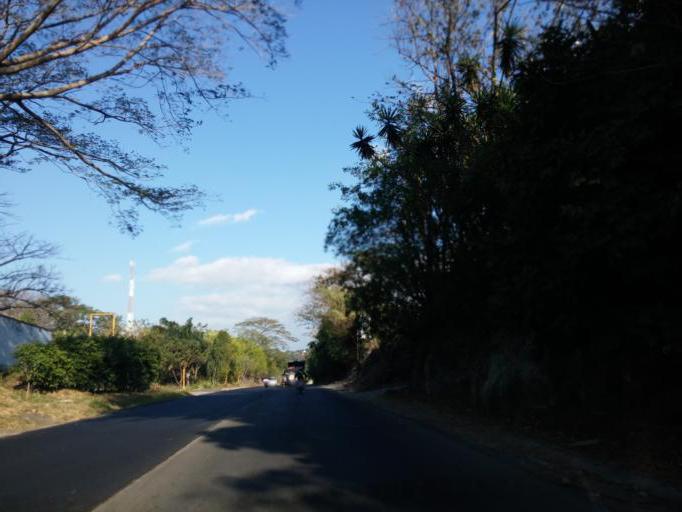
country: CR
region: Heredia
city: Colon
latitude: 9.9337
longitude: -84.2353
